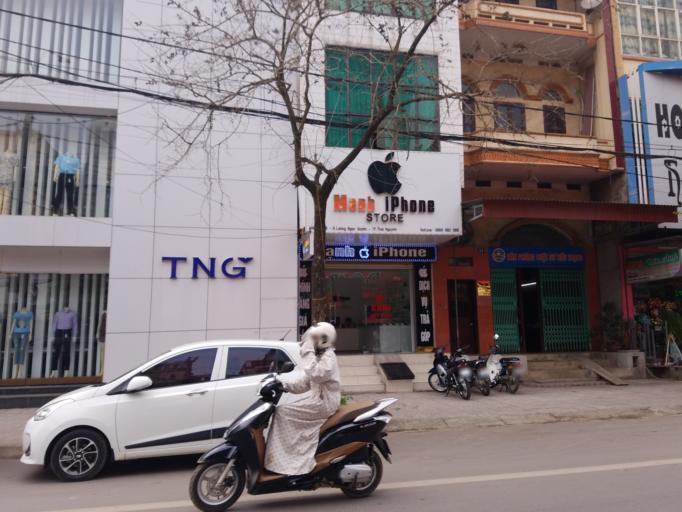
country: VN
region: Thai Nguyen
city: Thanh Pho Thai Nguyen
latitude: 21.5999
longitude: 105.8242
